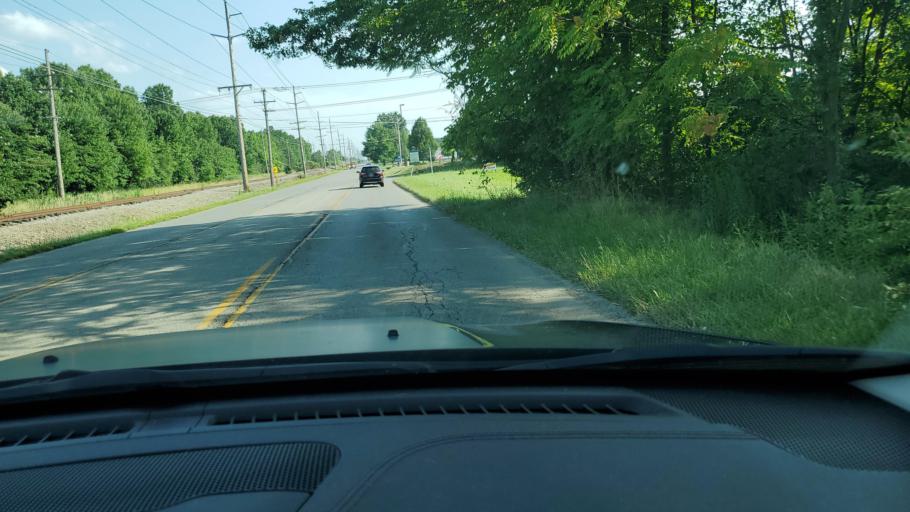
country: US
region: Ohio
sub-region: Mahoning County
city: Boardman
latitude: 41.0173
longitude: -80.6535
